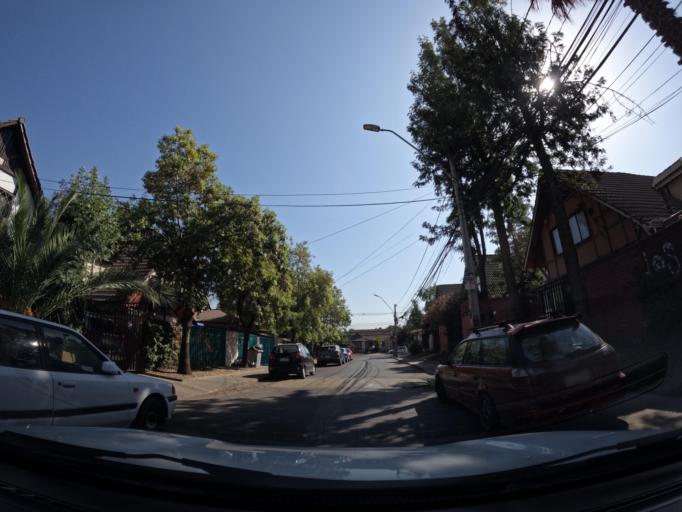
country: CL
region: Santiago Metropolitan
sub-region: Provincia de Santiago
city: Villa Presidente Frei, Nunoa, Santiago, Chile
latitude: -33.4809
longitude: -70.5537
